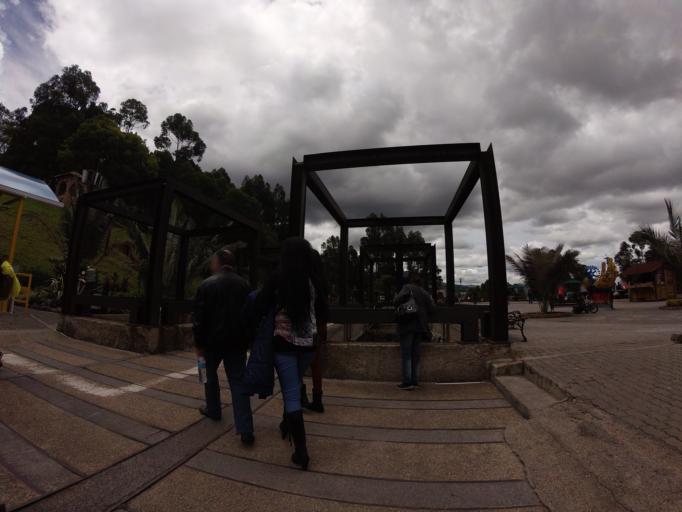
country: CO
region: Cundinamarca
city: Zipaquira
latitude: 5.0193
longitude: -74.0092
